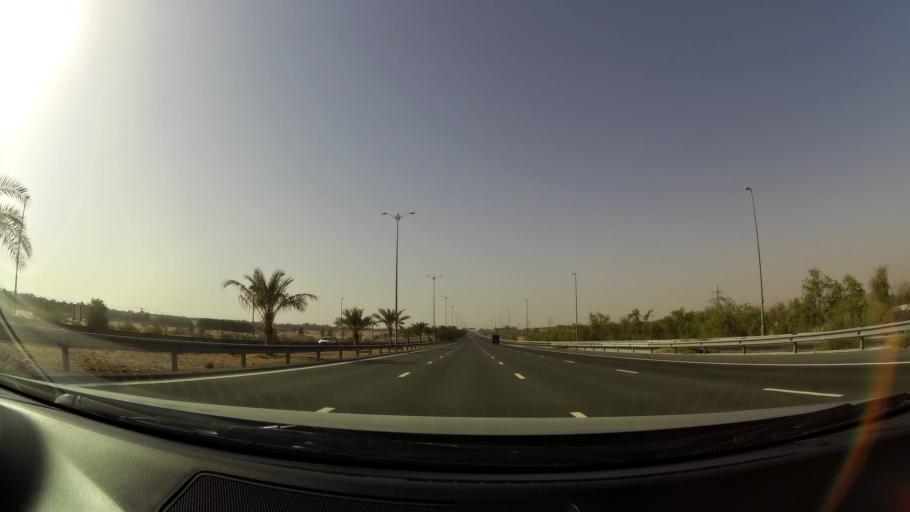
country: OM
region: Al Buraimi
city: Al Buraymi
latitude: 24.5697
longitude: 55.7480
